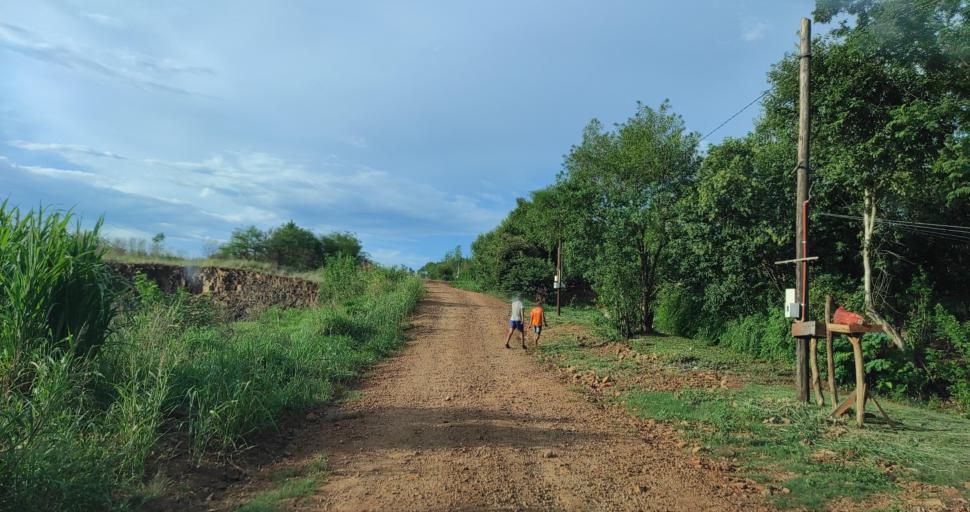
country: AR
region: Misiones
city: Santo Pipo
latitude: -27.1510
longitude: -55.4212
